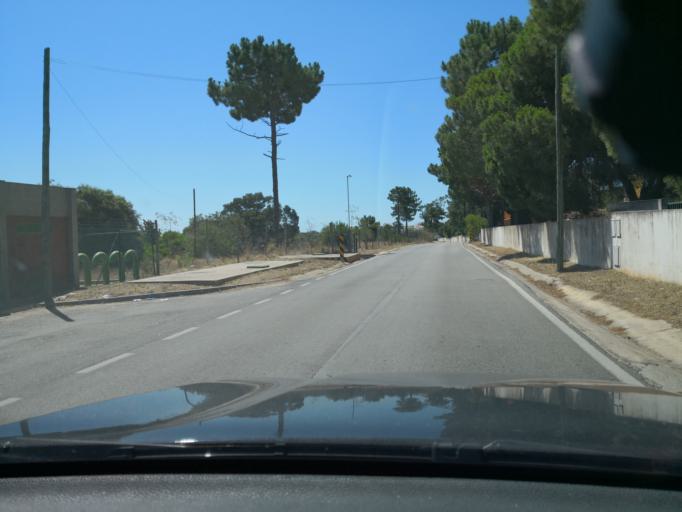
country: PT
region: Faro
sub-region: Loule
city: Quarteira
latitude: 37.0809
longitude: -8.0992
